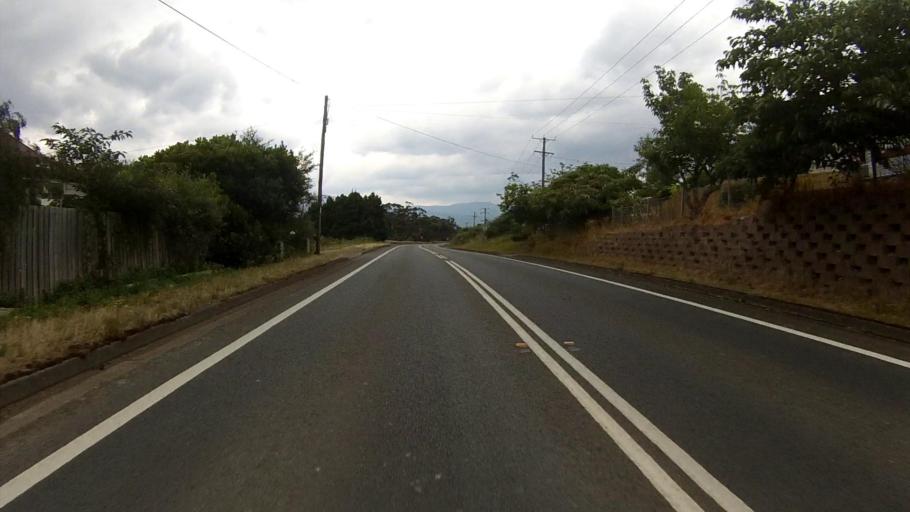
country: AU
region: Tasmania
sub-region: Huon Valley
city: Huonville
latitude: -43.0482
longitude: 147.0507
